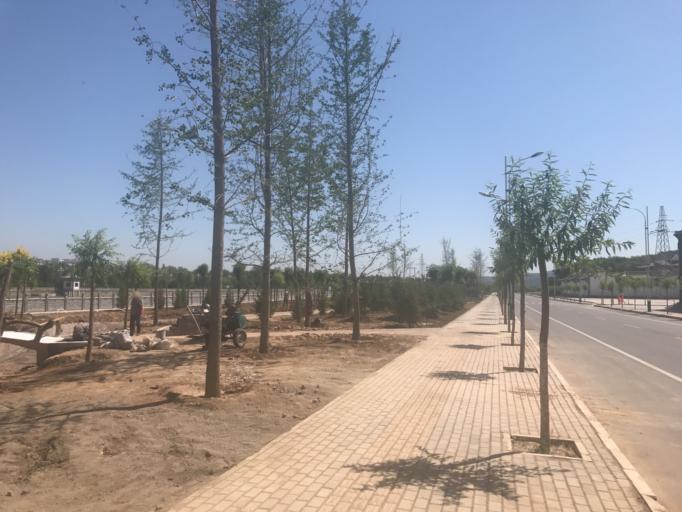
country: CN
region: Gansu Sheng
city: Hanji
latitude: 35.5020
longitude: 103.0875
